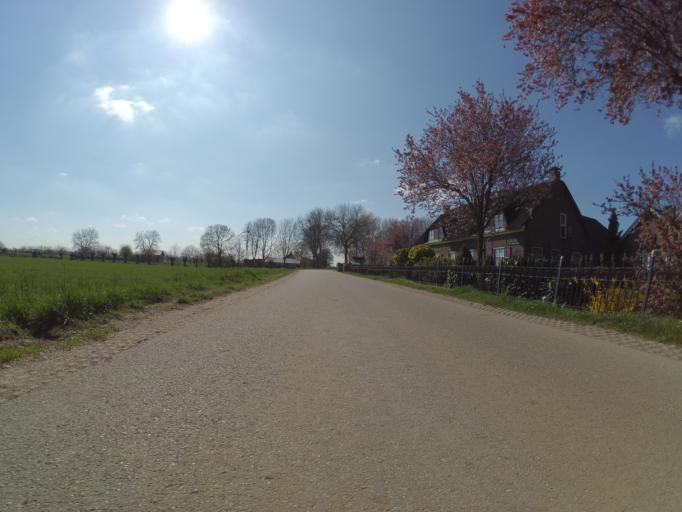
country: NL
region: Utrecht
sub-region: Gemeente Utrechtse Heuvelrug
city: Driebergen-Rijsenburg
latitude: 51.9992
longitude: 5.2723
